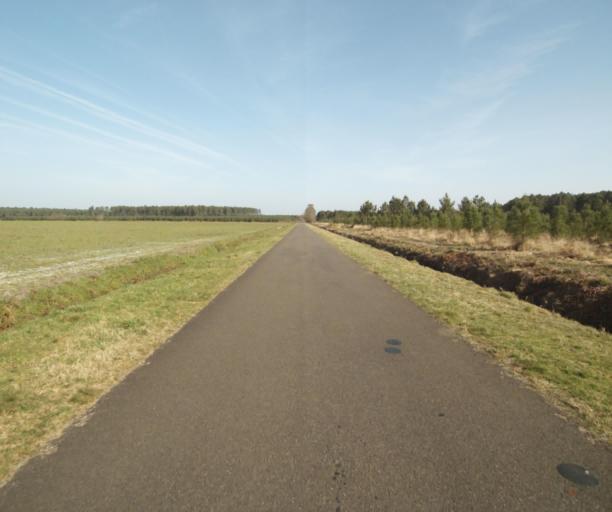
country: FR
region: Aquitaine
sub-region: Departement de la Gironde
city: Grignols
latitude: 44.1939
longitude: -0.1463
